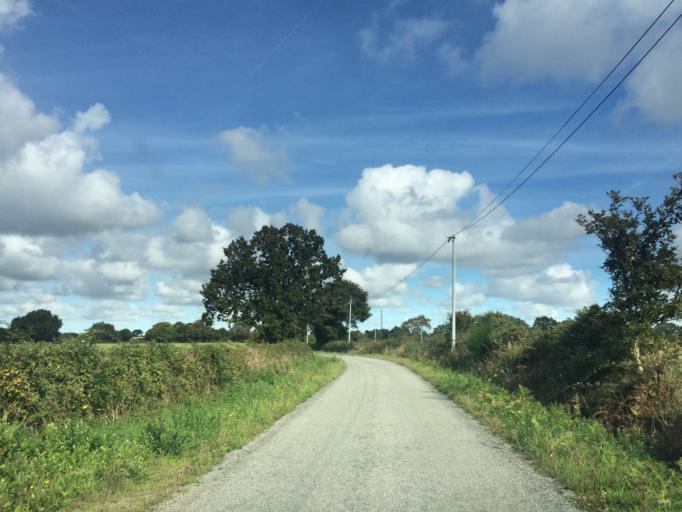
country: FR
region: Pays de la Loire
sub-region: Departement de la Loire-Atlantique
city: Chemere
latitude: 47.1191
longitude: -1.8915
